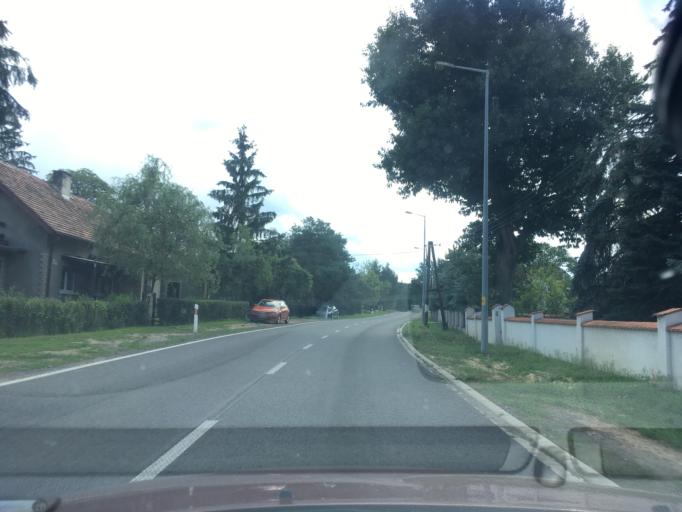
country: PL
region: Lower Silesian Voivodeship
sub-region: Powiat zgorzelecki
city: Piensk
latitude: 51.2242
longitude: 15.0267
